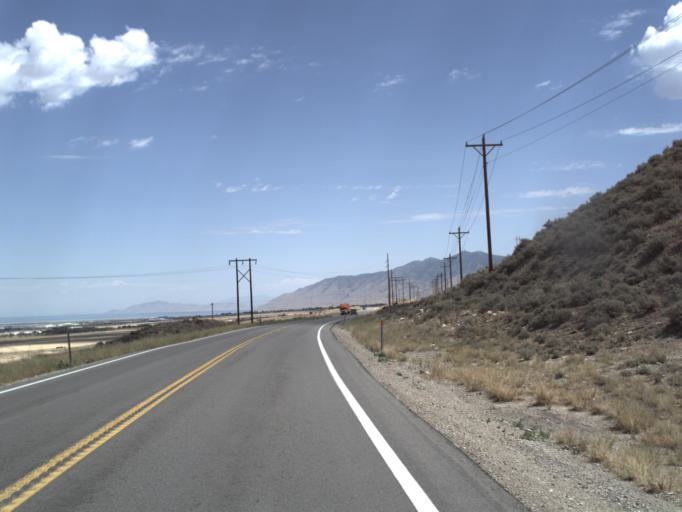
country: US
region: Utah
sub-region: Tooele County
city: Tooele
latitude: 40.4673
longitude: -112.3525
